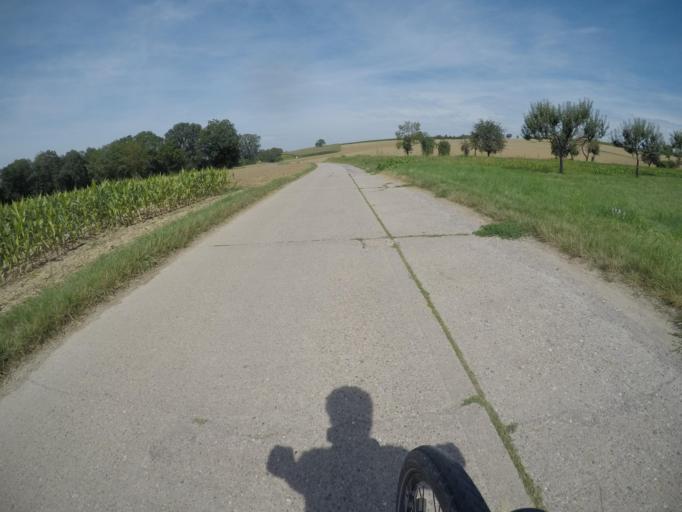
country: DE
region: Baden-Wuerttemberg
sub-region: Karlsruhe Region
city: Gondelsheim
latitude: 49.0486
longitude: 8.6726
